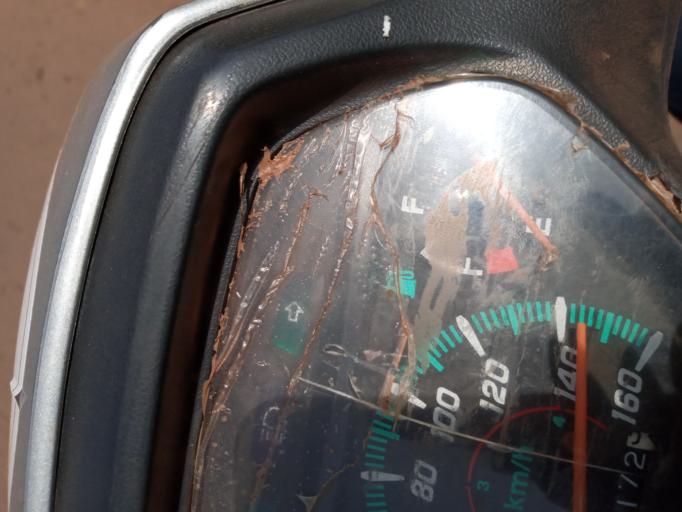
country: ML
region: Bamako
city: Bamako
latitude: 12.5613
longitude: -7.9808
